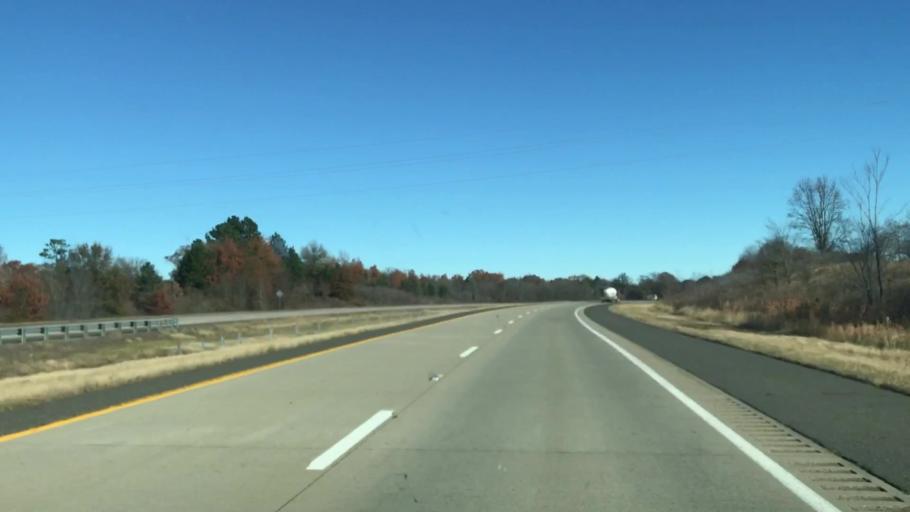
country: US
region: Texas
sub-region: Cass County
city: Queen City
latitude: 33.1542
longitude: -93.8897
